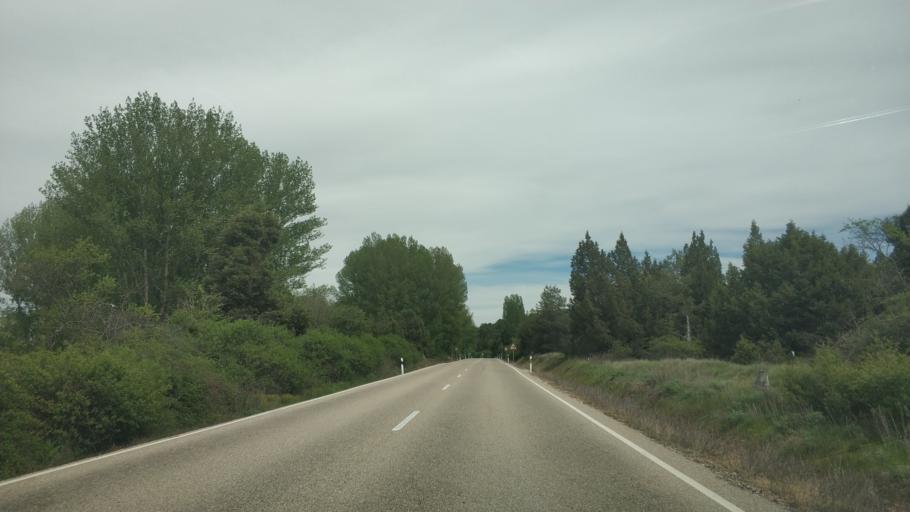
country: ES
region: Castille and Leon
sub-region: Provincia de Soria
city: Valdenebro
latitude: 41.5657
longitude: -2.9971
